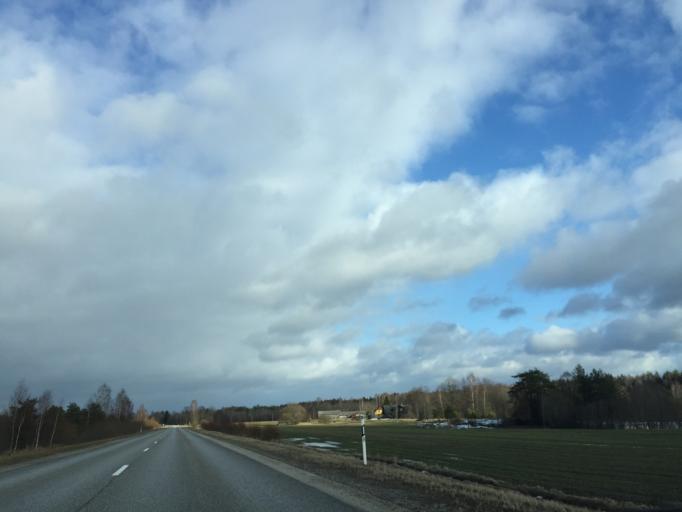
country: LV
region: Aloja
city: Staicele
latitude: 57.8797
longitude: 24.5929
